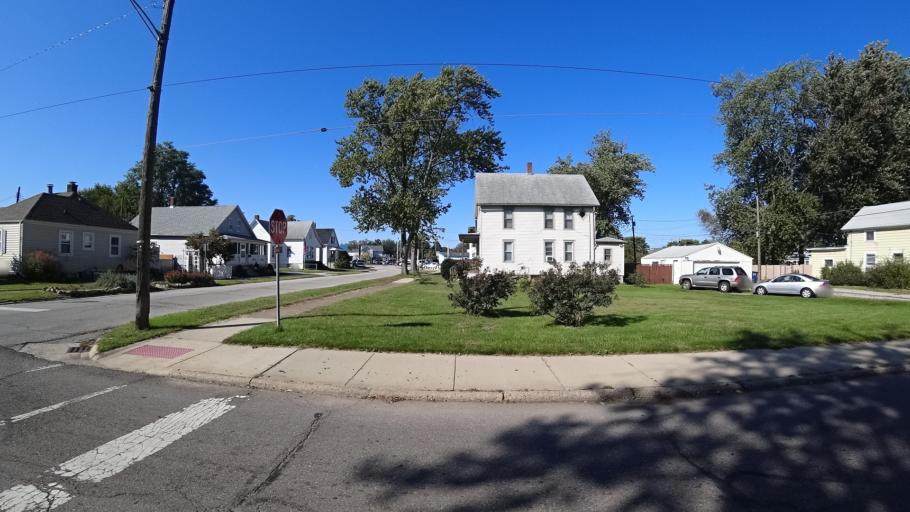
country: US
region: Indiana
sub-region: LaPorte County
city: Michigan City
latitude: 41.7040
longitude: -86.8936
